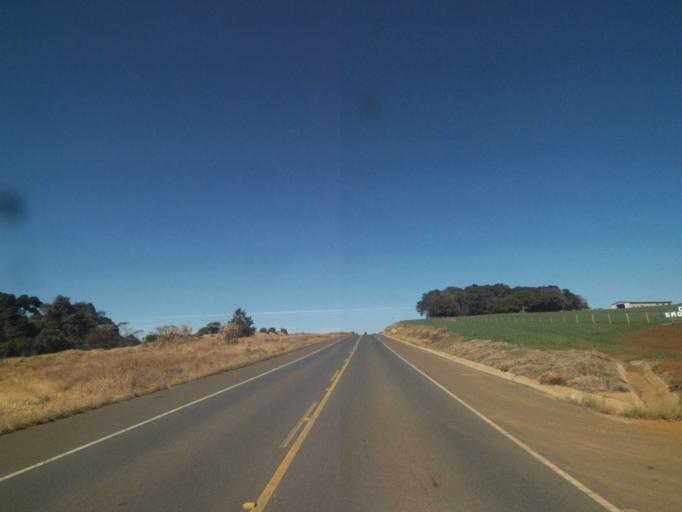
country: BR
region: Parana
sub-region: Tibagi
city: Tibagi
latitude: -24.5368
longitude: -50.4471
